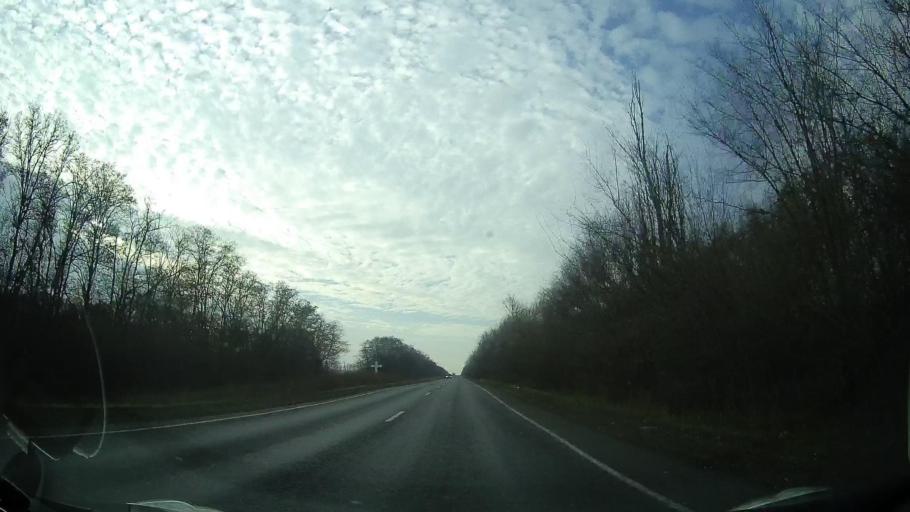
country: RU
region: Rostov
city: Bagayevskaya
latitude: 47.0960
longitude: 40.2994
